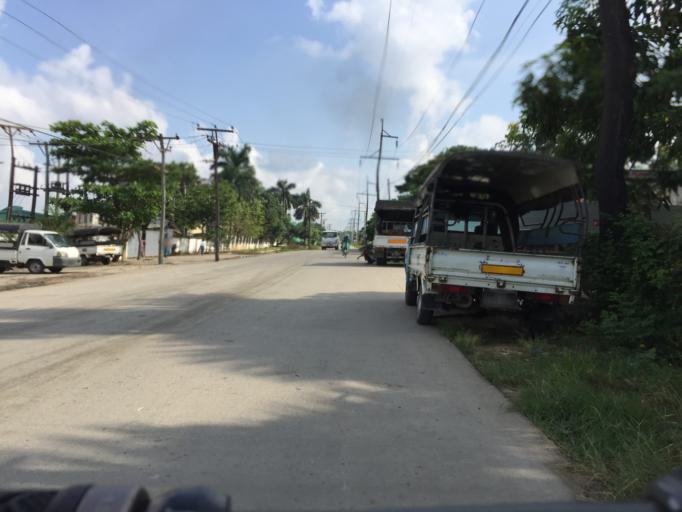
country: MM
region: Yangon
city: Syriam
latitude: 16.8290
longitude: 96.2237
